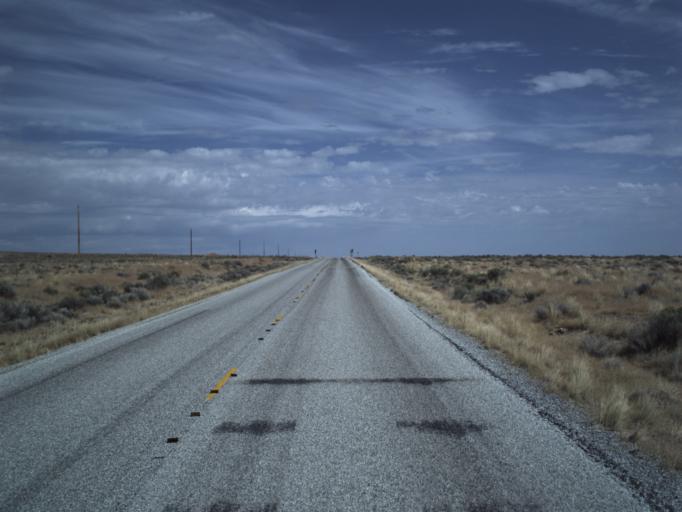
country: US
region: Utah
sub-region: Tooele County
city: Wendover
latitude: 41.4855
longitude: -113.6244
